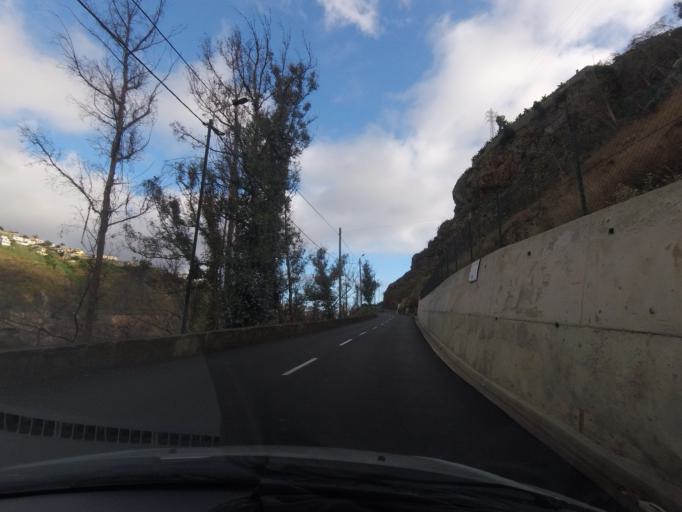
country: PT
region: Madeira
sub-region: Funchal
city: Nossa Senhora do Monte
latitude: 32.6736
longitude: -16.9183
